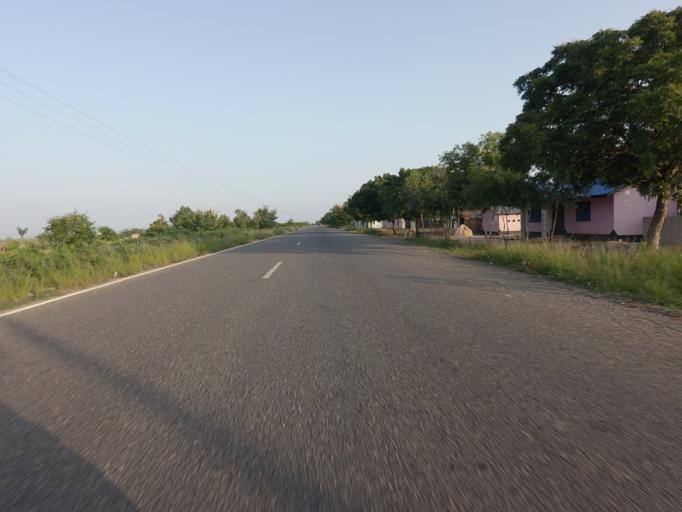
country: GH
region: Volta
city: Anloga
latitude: 5.9056
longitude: 0.7112
